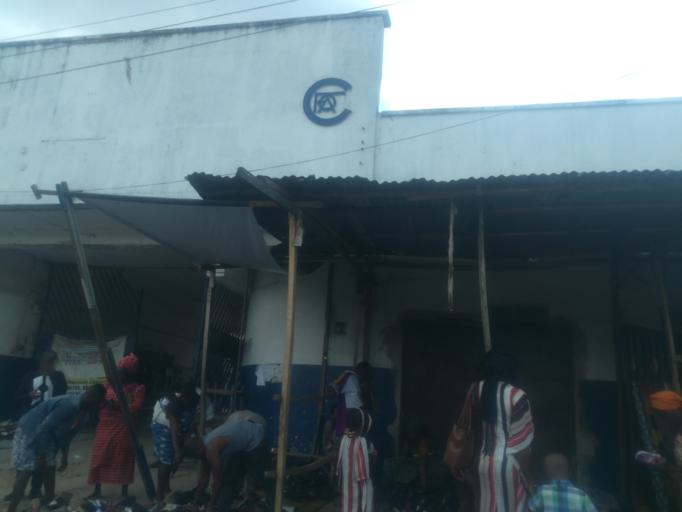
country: NG
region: Oyo
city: Ibadan
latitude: 7.3893
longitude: 3.8826
